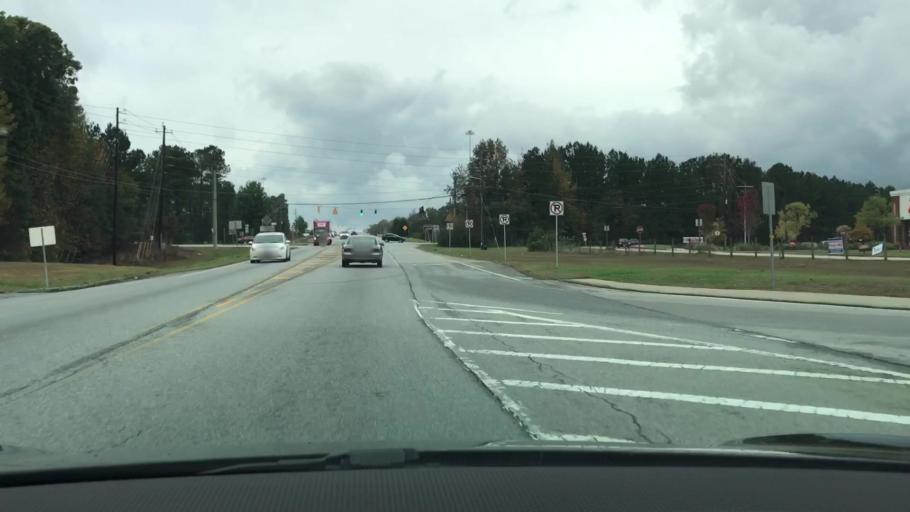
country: US
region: Georgia
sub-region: Greene County
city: Greensboro
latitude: 33.5480
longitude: -83.2035
